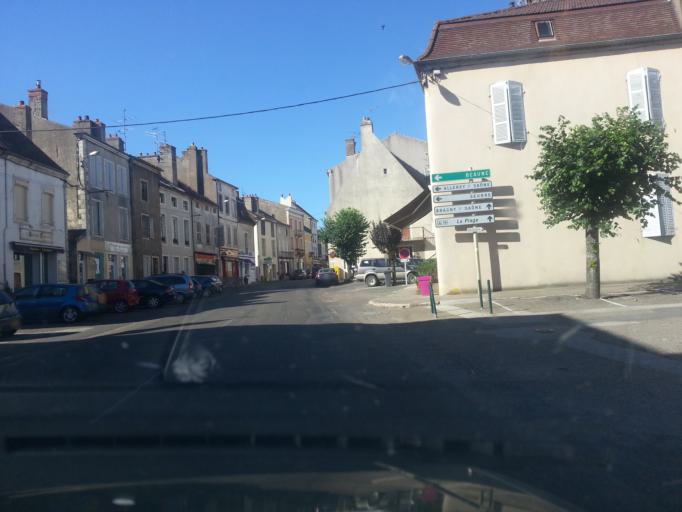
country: FR
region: Bourgogne
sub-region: Departement de Saone-et-Loire
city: Verdun-sur-le-Doubs
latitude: 46.8949
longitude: 5.0240
